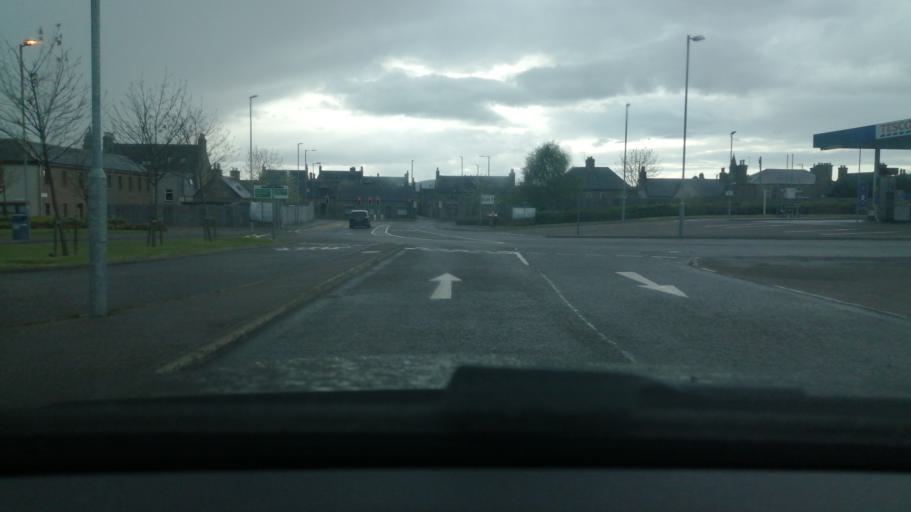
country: GB
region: Scotland
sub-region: Moray
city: Keith
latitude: 57.5417
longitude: -2.9460
